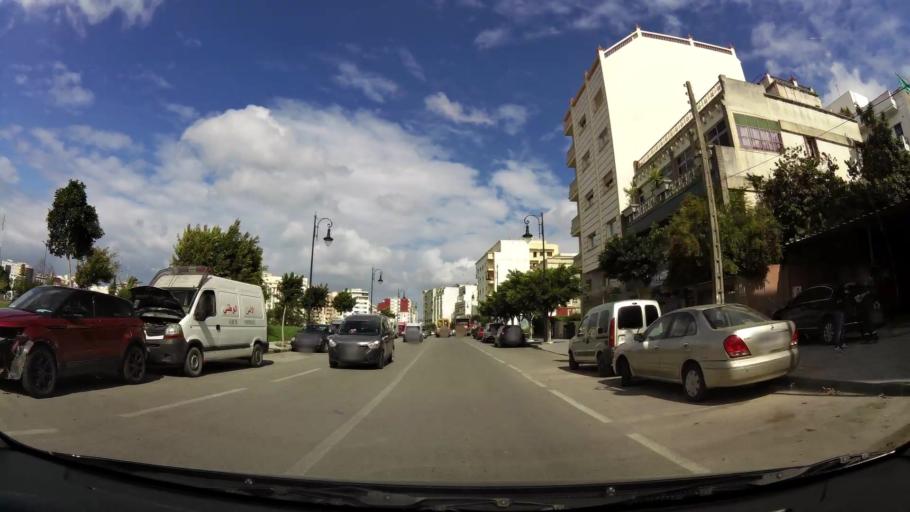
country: MA
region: Tanger-Tetouan
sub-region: Tanger-Assilah
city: Tangier
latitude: 35.7642
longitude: -5.8130
